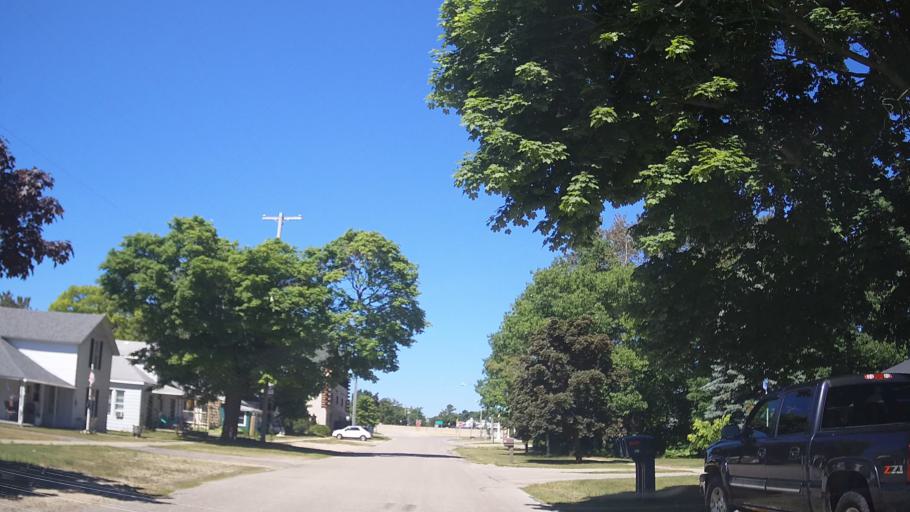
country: US
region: Michigan
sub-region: Mackinac County
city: Saint Ignace
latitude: 45.7837
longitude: -84.7303
